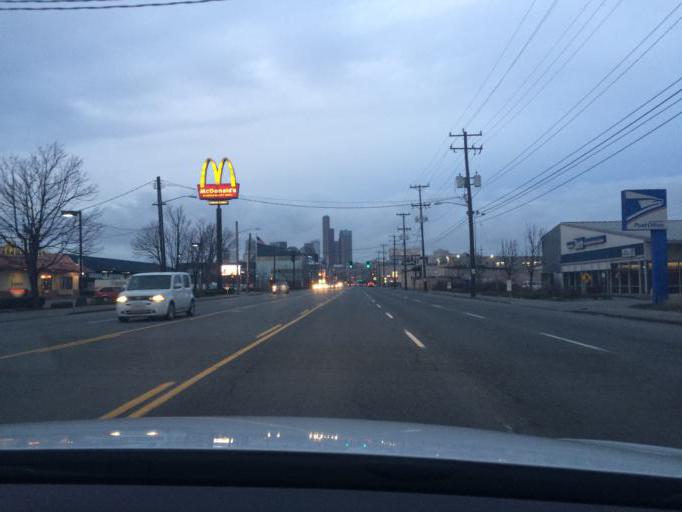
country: US
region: Washington
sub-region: King County
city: Seattle
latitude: 47.5810
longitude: -122.3290
